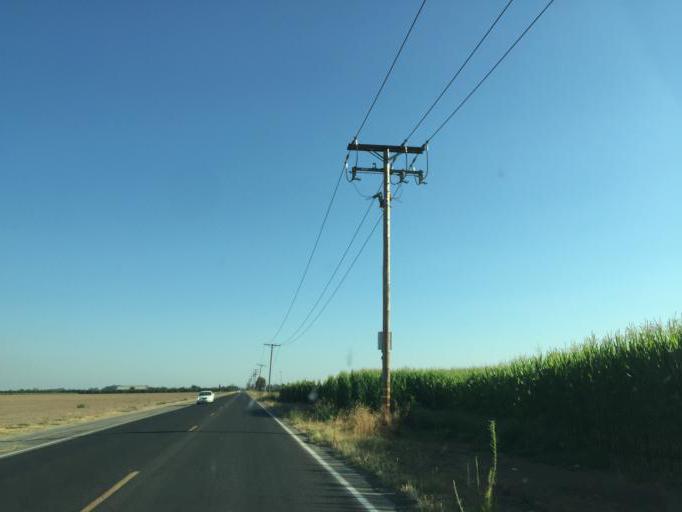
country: US
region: California
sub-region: Tulare County
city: Ivanhoe
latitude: 36.4137
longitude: -119.2781
